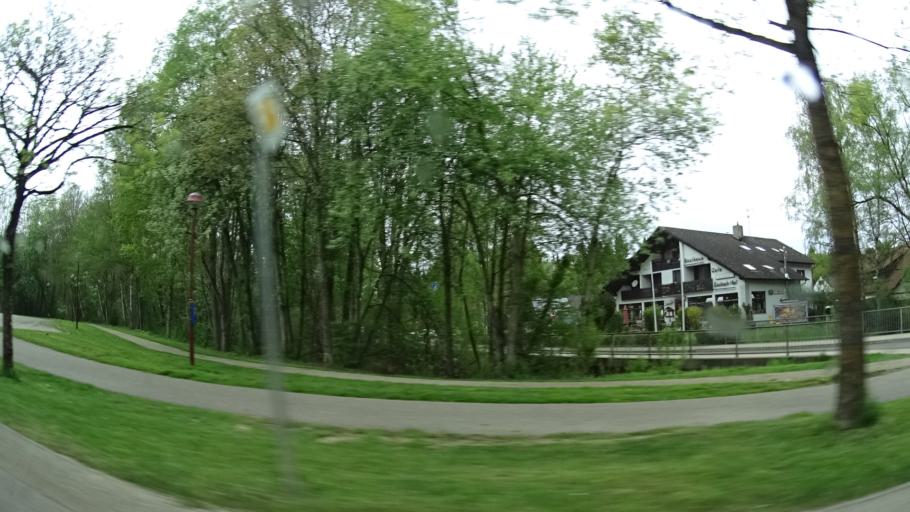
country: DE
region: Baden-Wuerttemberg
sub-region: Freiburg Region
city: Niedereschach
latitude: 48.1289
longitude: 8.5259
